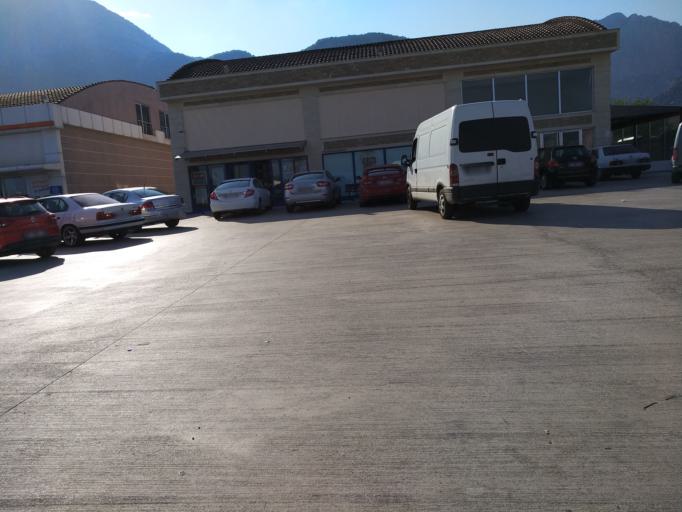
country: TR
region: Antalya
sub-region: Kemer
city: Goeynuek
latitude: 36.6660
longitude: 30.5509
